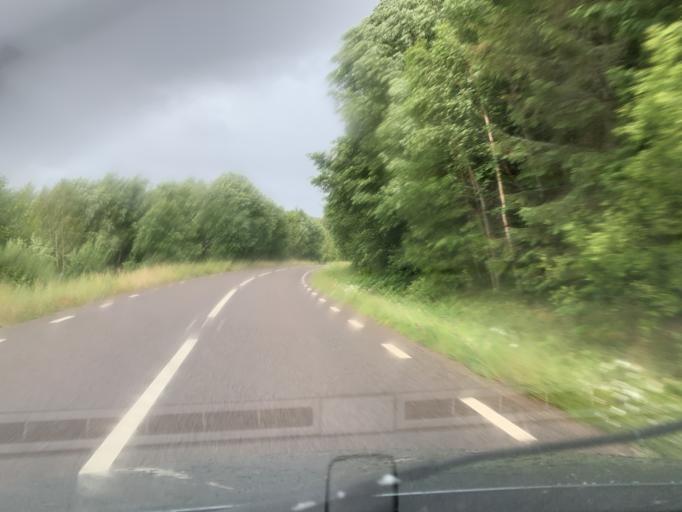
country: SE
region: Kalmar
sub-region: Vasterviks Kommun
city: Overum
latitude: 58.0174
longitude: 16.1545
